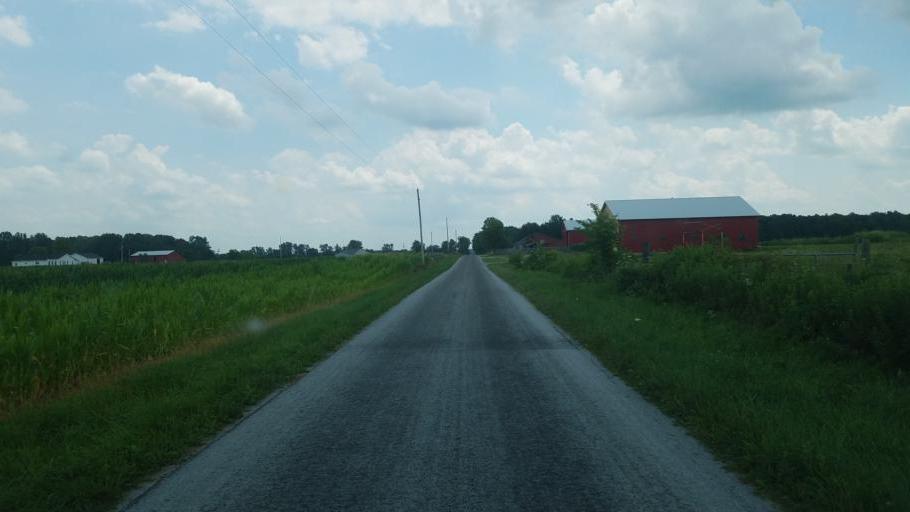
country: US
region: Ohio
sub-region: Hardin County
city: Kenton
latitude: 40.5645
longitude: -83.4870
